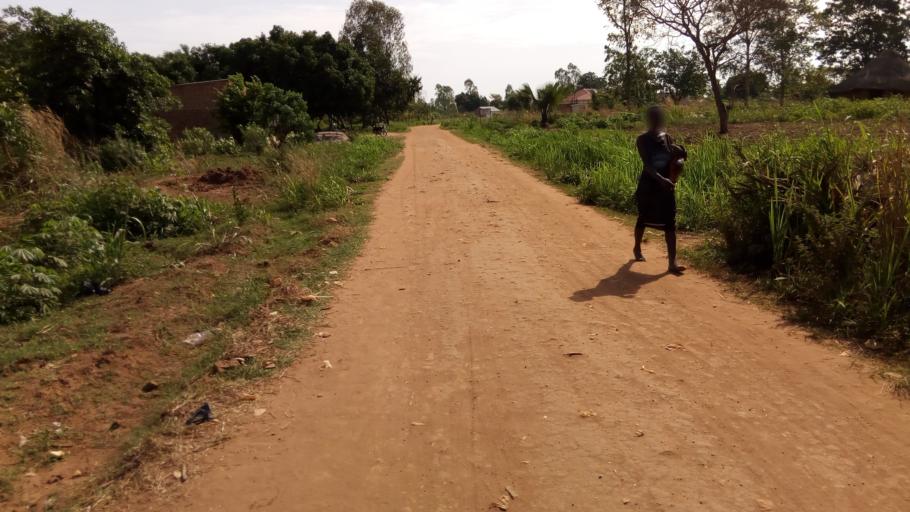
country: UG
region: Northern Region
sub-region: Gulu District
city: Gulu
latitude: 2.7942
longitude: 32.3259
